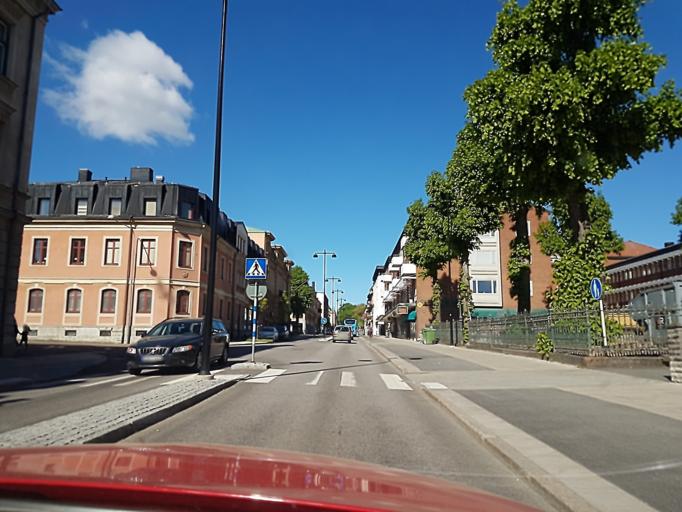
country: SE
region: Vaestra Goetaland
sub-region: Skovde Kommun
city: Skoevde
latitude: 58.3881
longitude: 13.8483
